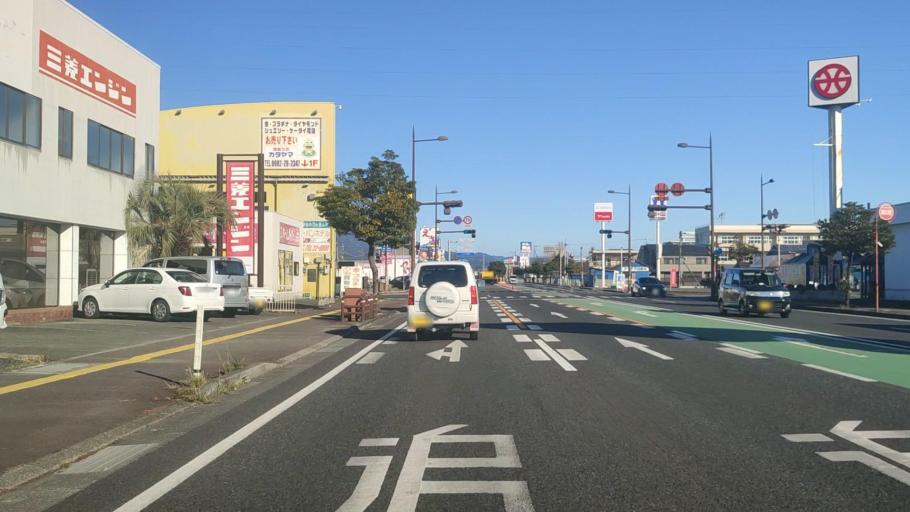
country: JP
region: Miyazaki
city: Nobeoka
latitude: 32.5713
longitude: 131.6836
